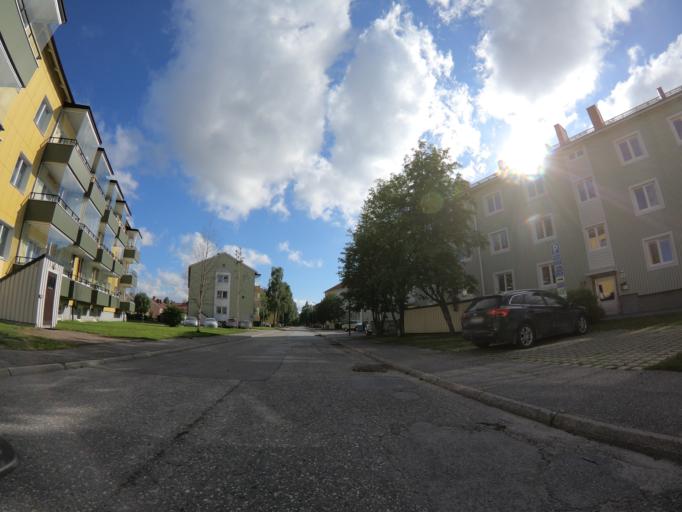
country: SE
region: Vaesterbotten
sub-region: Umea Kommun
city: Umea
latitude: 63.8341
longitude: 20.2774
